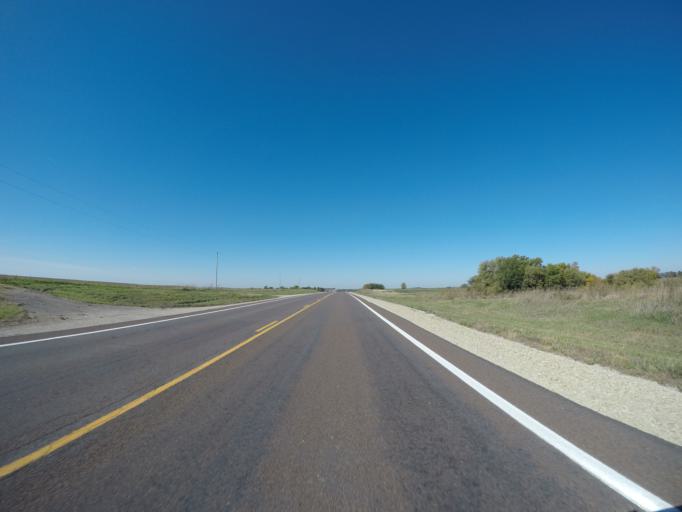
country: US
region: Kansas
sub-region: Riley County
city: Fort Riley North
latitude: 39.3065
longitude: -96.8742
